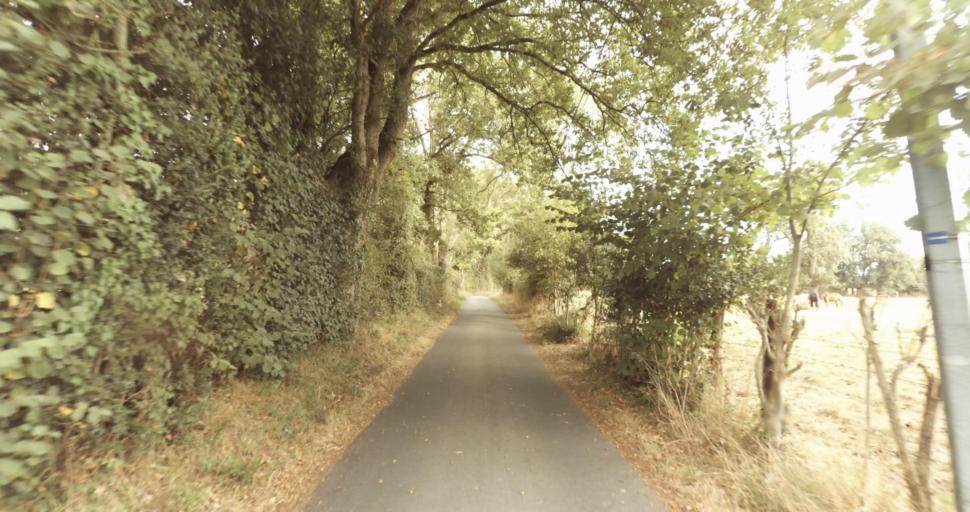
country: FR
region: Lower Normandy
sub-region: Departement de l'Orne
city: Vimoutiers
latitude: 48.9554
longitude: 0.2491
